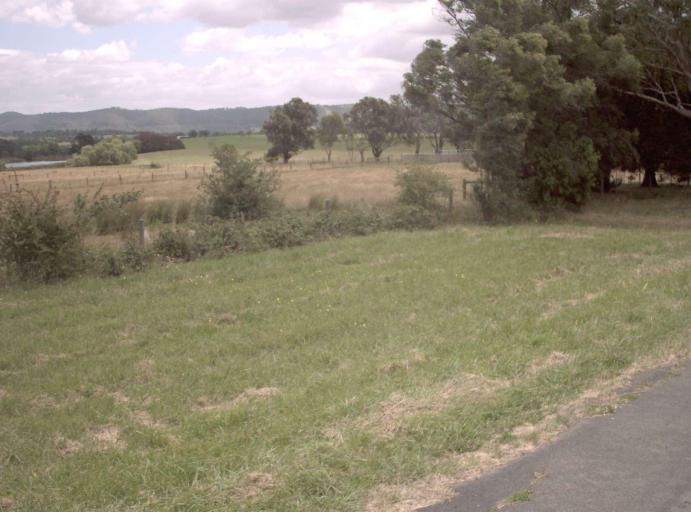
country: AU
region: Victoria
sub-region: Yarra Ranges
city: Lilydale
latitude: -37.7159
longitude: 145.3868
